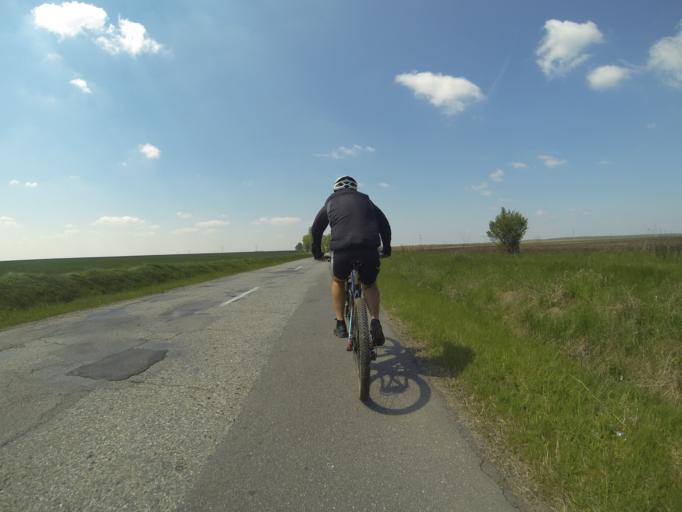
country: RO
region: Dolj
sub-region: Comuna Predesti
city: Predesti
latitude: 44.2994
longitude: 23.5715
